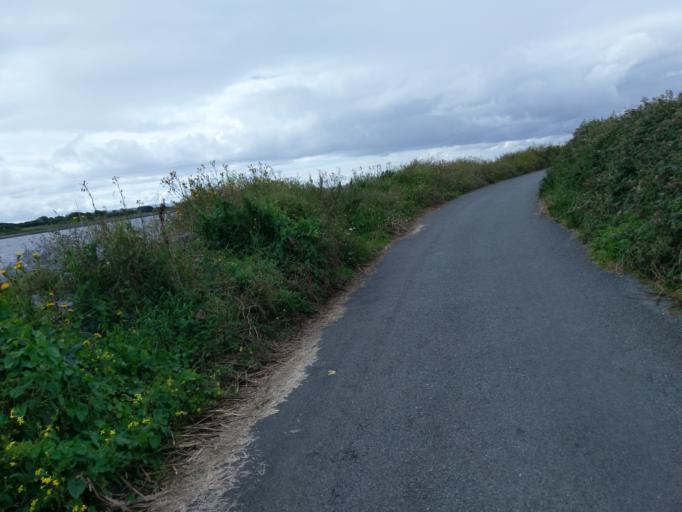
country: IE
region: Connaught
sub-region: County Galway
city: Oranmore
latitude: 53.2439
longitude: -8.9702
